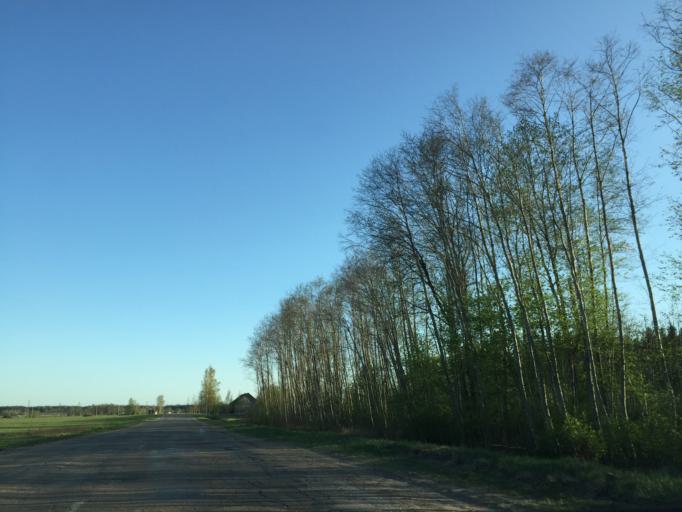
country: LV
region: Koknese
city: Koknese
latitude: 56.6904
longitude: 25.4870
